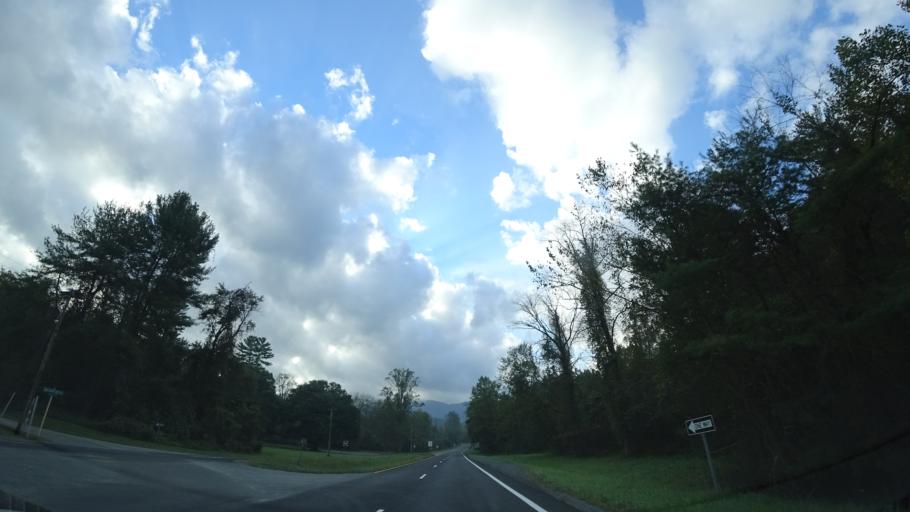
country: US
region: Virginia
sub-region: Page County
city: Luray
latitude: 38.6635
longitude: -78.3735
